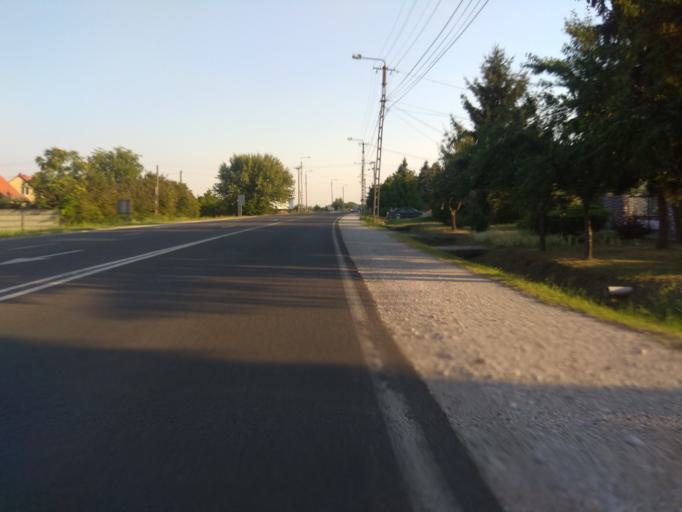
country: HU
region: Borsod-Abauj-Zemplen
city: Nyekladhaza
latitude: 47.9857
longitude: 20.8313
